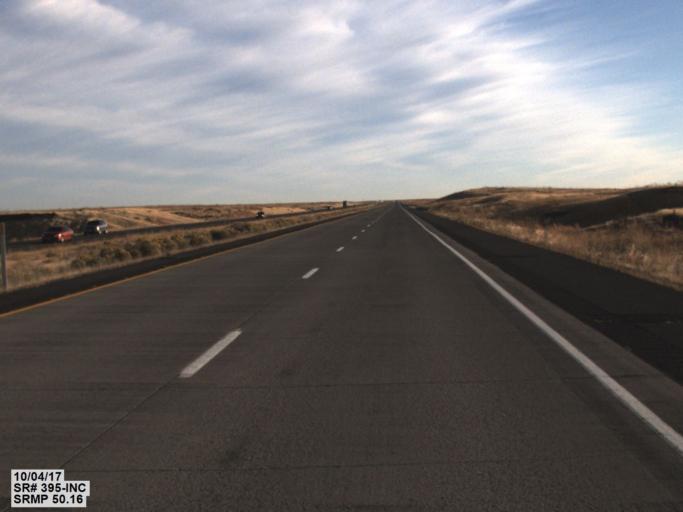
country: US
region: Washington
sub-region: Franklin County
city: Connell
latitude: 46.6043
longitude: -118.9234
